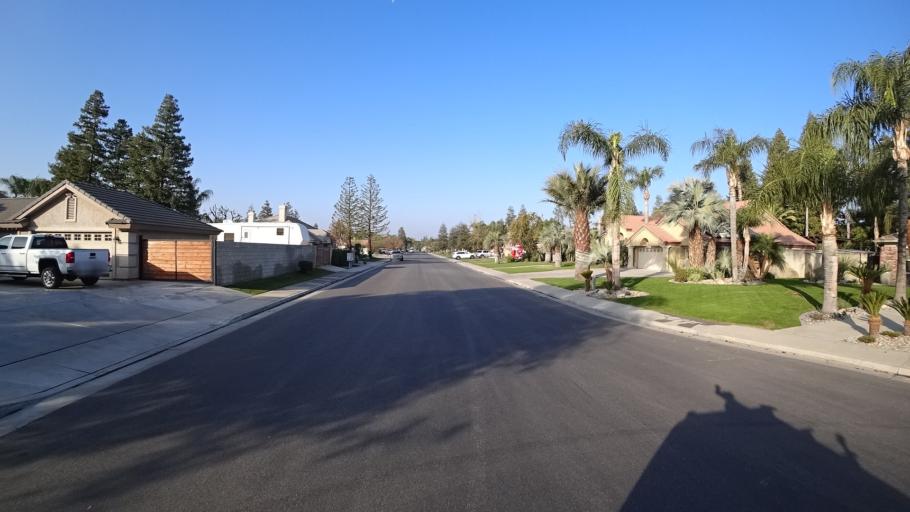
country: US
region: California
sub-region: Kern County
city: Rosedale
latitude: 35.3721
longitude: -119.1379
